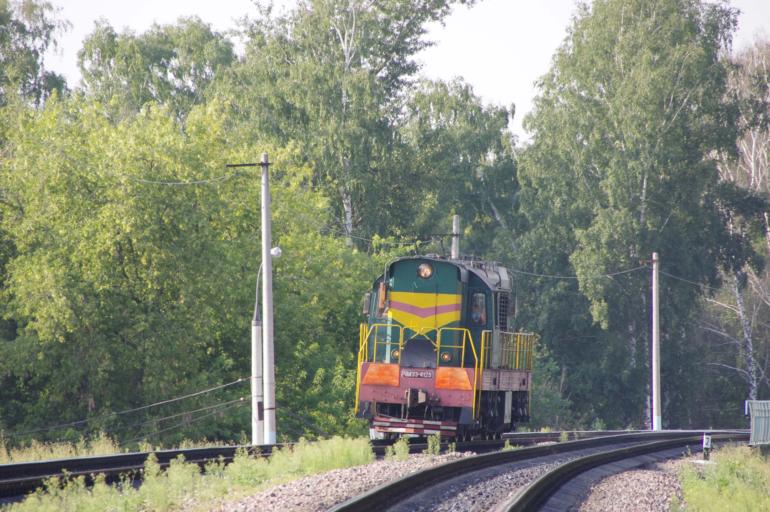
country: RU
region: Moscow
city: Pokrovskoye-Streshnevo
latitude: 55.8152
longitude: 37.4868
